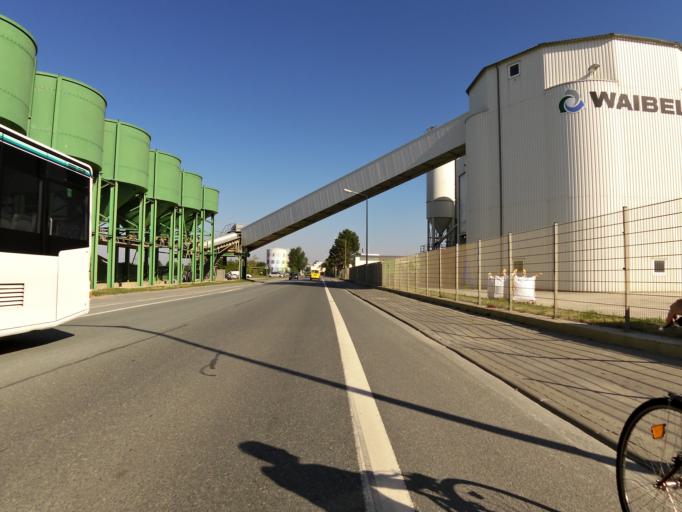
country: DE
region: Hesse
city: Gernsheim
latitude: 49.7651
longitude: 8.4816
